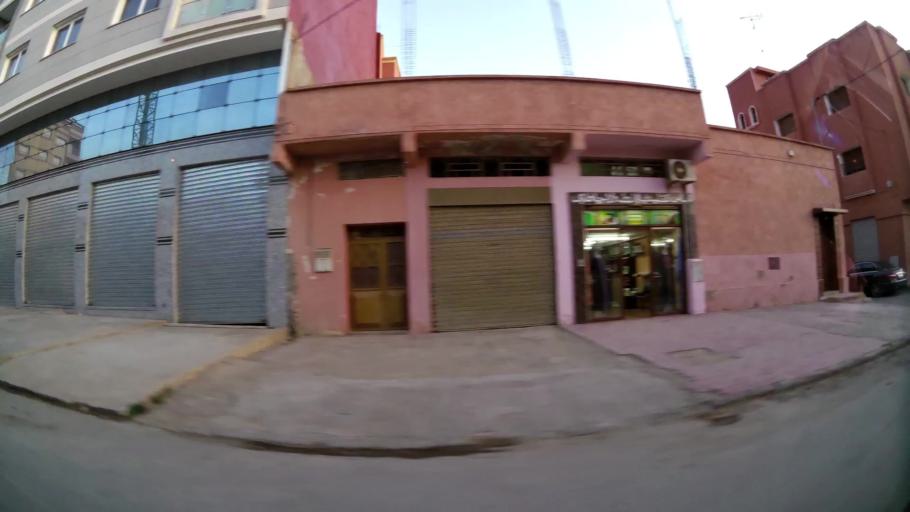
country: MA
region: Oriental
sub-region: Berkane-Taourirt
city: Berkane
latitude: 34.9211
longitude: -2.3266
